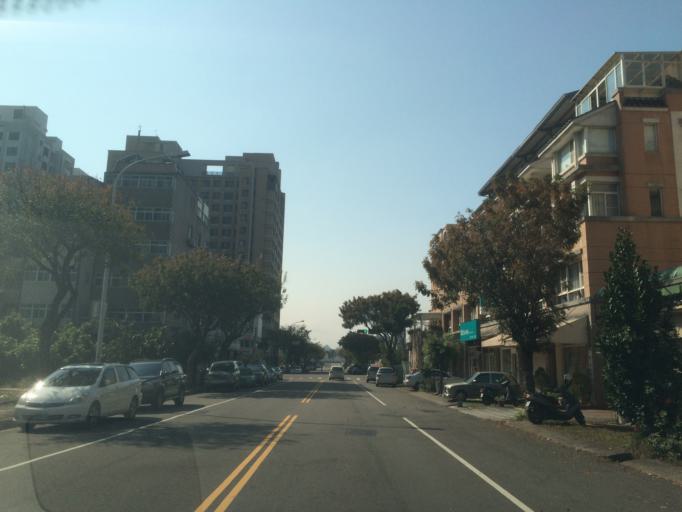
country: TW
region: Taiwan
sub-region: Taichung City
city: Taichung
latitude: 24.1782
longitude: 120.7143
